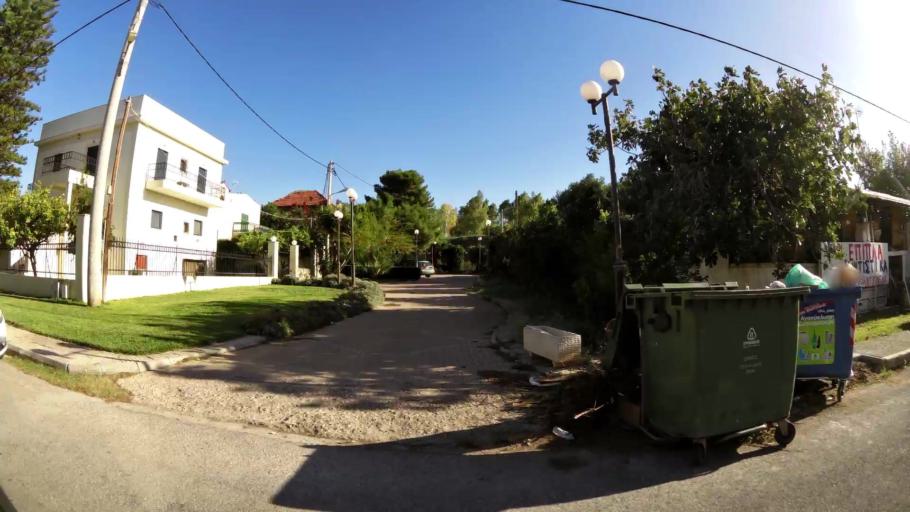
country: GR
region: Attica
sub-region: Nomarchia Athinas
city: Elliniko
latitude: 37.8751
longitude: 23.7364
